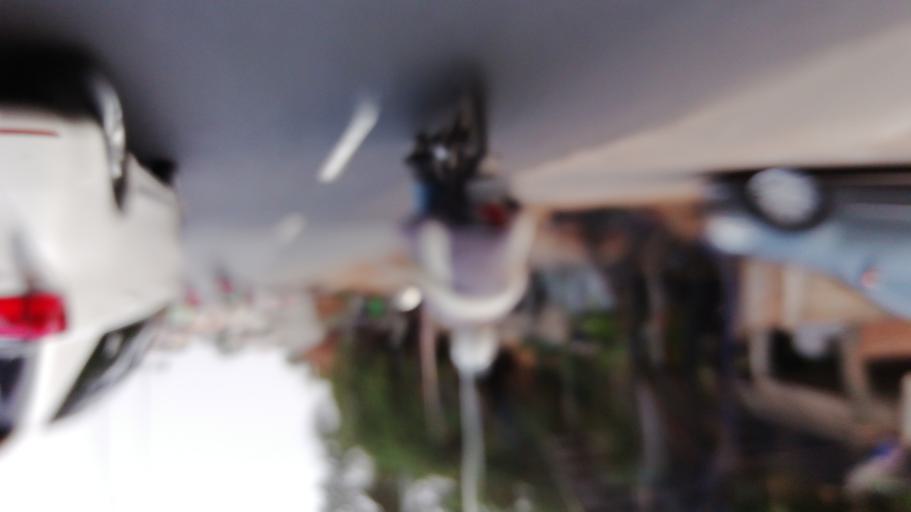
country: ID
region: West Java
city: Pamulang
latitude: -6.2907
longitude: 106.8052
